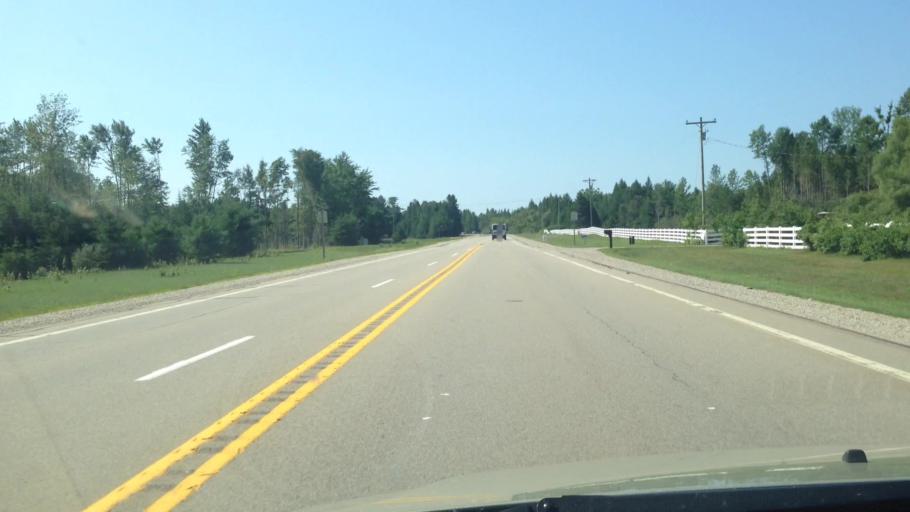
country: US
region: Michigan
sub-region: Delta County
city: Escanaba
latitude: 45.5258
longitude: -87.2875
